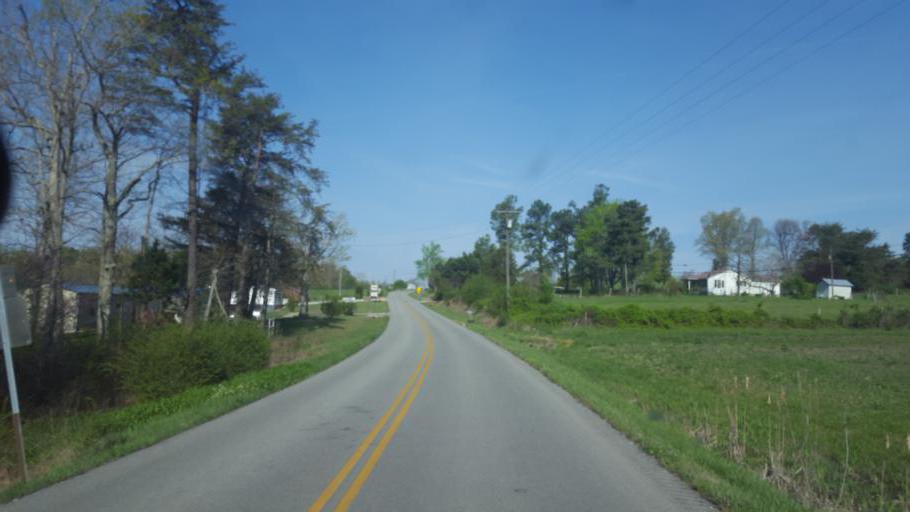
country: US
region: Kentucky
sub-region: Edmonson County
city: Brownsville
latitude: 37.2699
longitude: -86.1622
